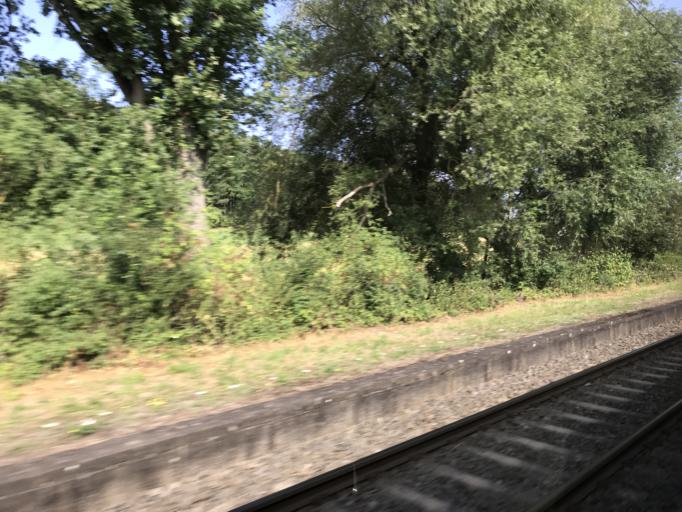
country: DE
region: Hesse
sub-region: Regierungsbezirk Giessen
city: Runkel
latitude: 50.3757
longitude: 8.1334
